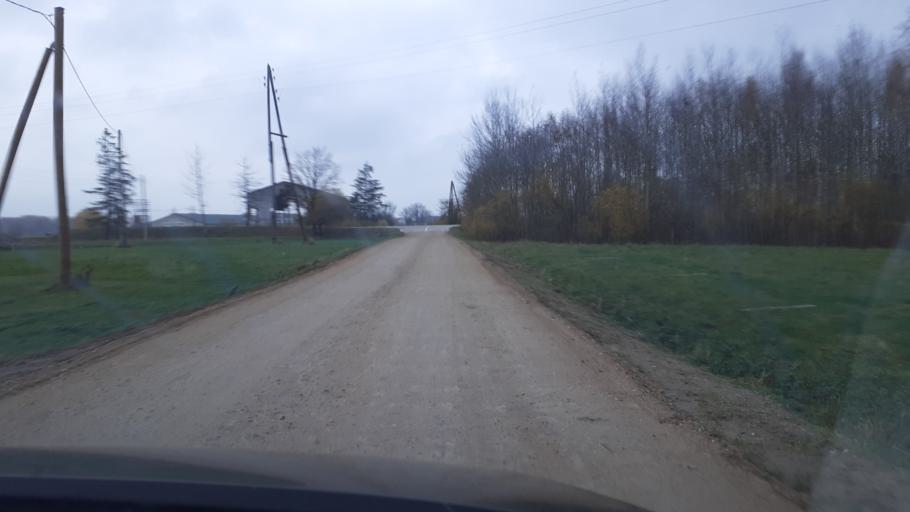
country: LV
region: Talsu Rajons
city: Sabile
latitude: 56.9419
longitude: 22.4205
